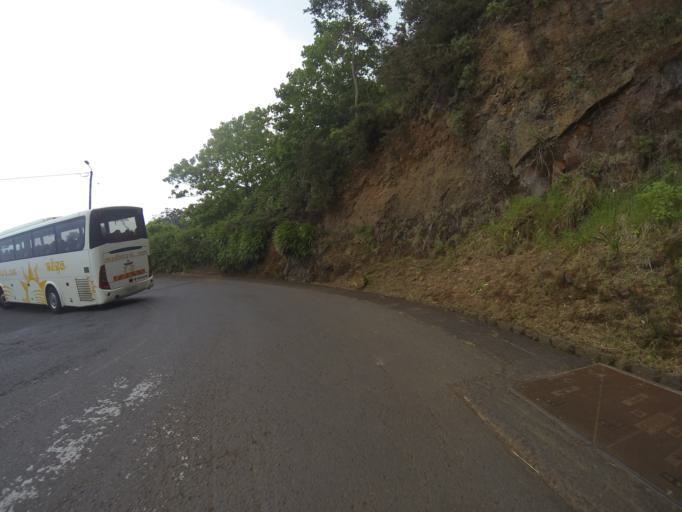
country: PT
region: Madeira
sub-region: Porto Moniz
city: Porto Moniz
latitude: 32.8621
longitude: -17.1728
